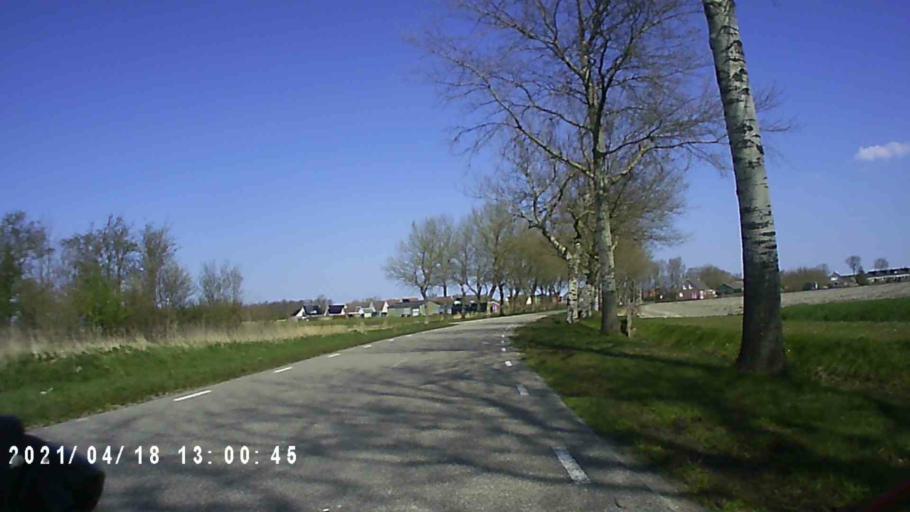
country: NL
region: Friesland
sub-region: Gemeente Dongeradeel
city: Anjum
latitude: 53.3985
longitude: 6.0859
